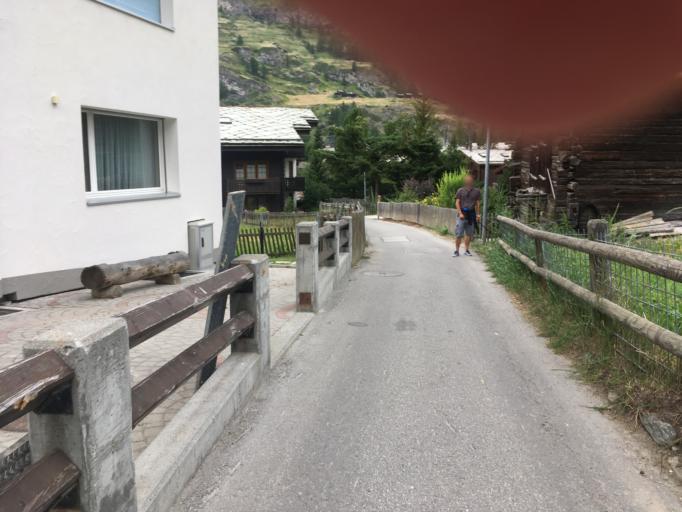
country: CH
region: Valais
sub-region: Visp District
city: Zermatt
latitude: 46.0126
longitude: 7.7466
